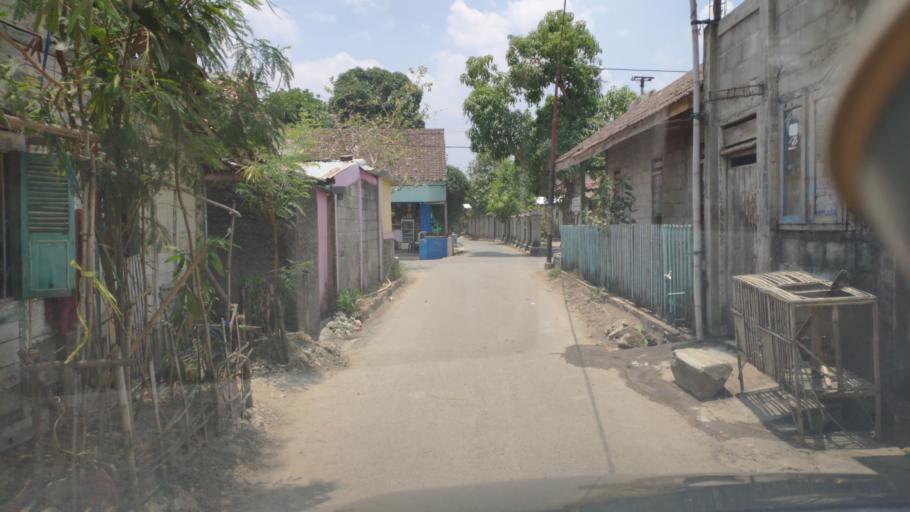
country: ID
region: Central Java
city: Beran
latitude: -6.9796
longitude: 111.4054
